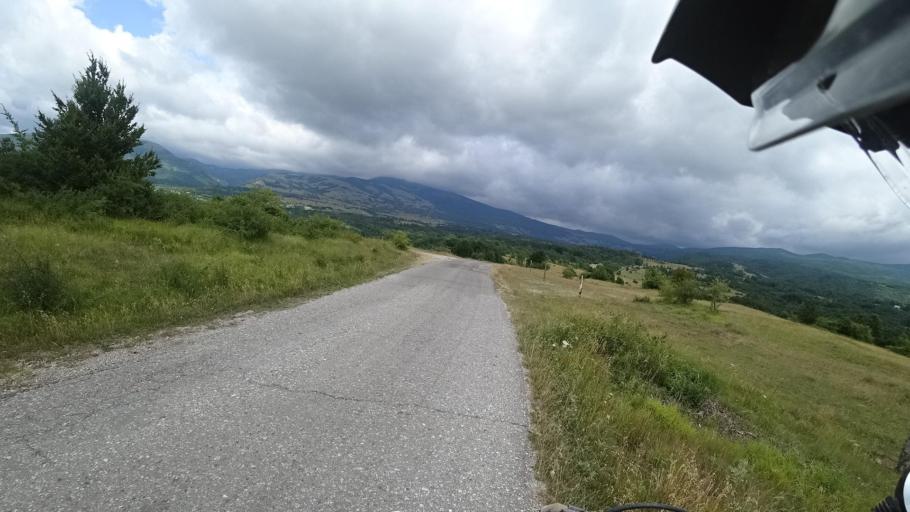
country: HR
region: Zadarska
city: Gracac
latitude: 44.5262
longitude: 15.7947
